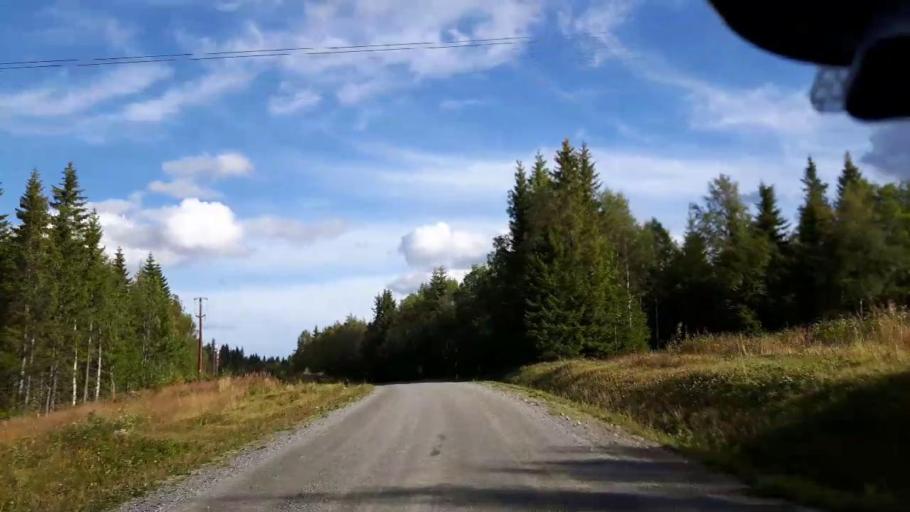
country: SE
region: Jaemtland
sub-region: Ragunda Kommun
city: Hammarstrand
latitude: 63.4424
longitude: 15.9787
